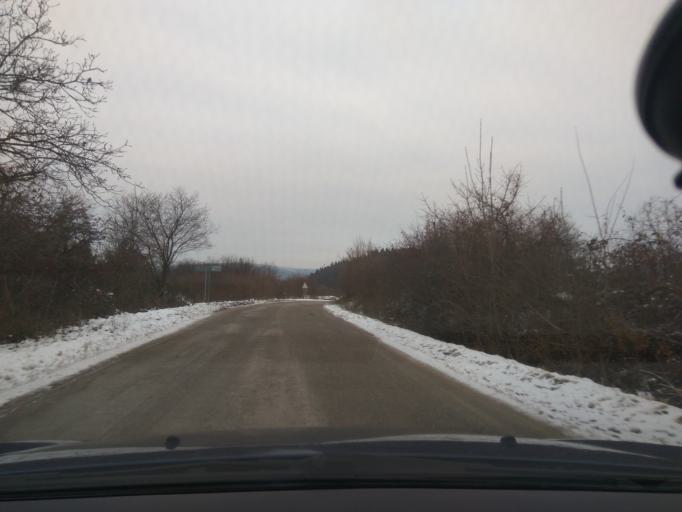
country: SK
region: Nitriansky
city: Stara Tura
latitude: 48.8133
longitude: 17.7070
